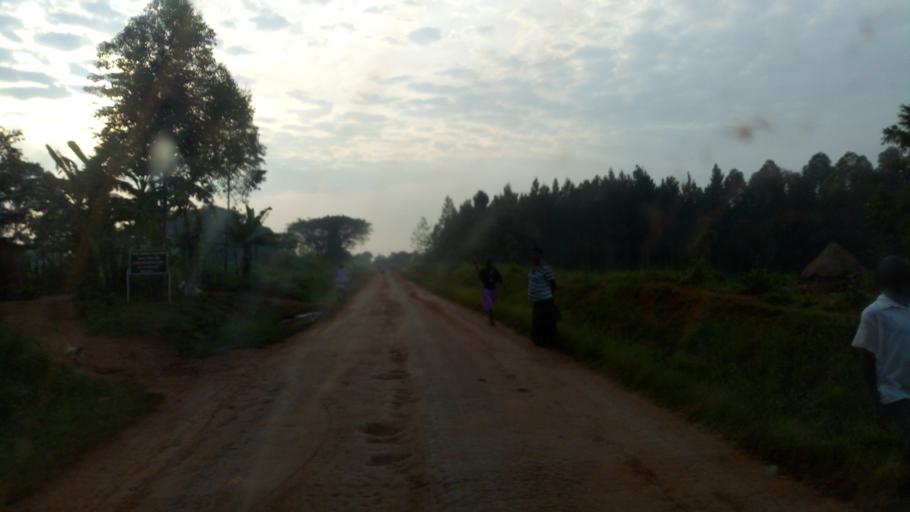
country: UG
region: Western Region
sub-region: Masindi District
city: Masindi
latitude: 1.6734
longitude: 31.7586
